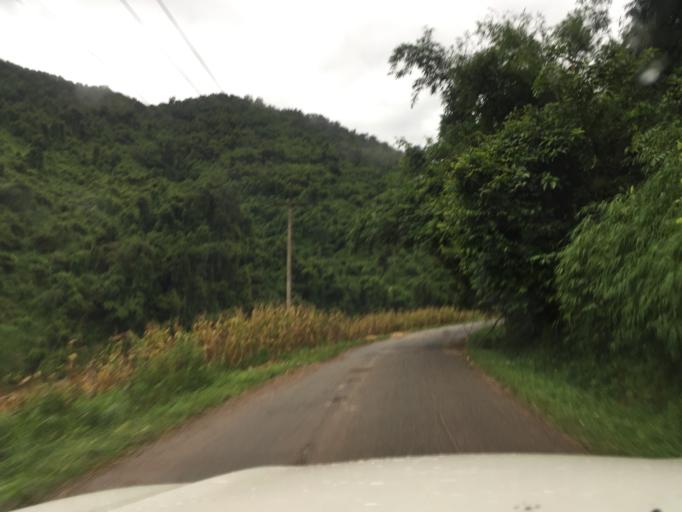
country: LA
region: Oudomxai
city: Muang La
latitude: 20.9512
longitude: 102.2143
